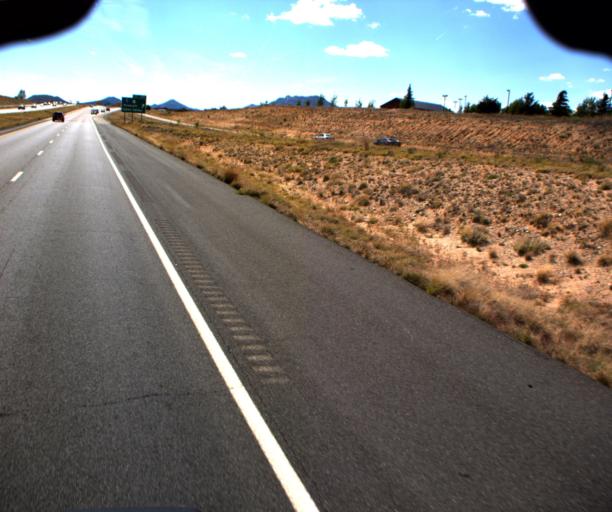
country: US
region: Arizona
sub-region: Yavapai County
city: Prescott Valley
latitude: 34.6348
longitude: -112.4188
